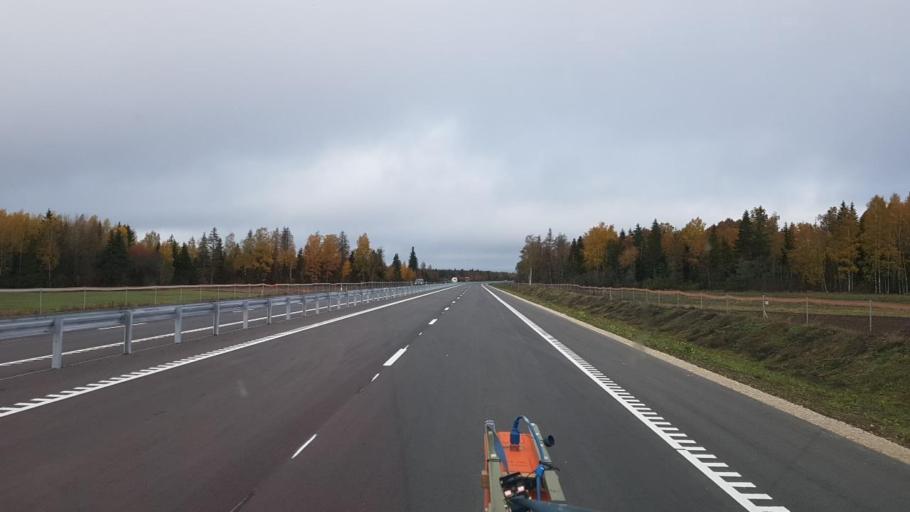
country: EE
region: Jaervamaa
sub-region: Paide linn
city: Paide
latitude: 59.0051
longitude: 25.5685
